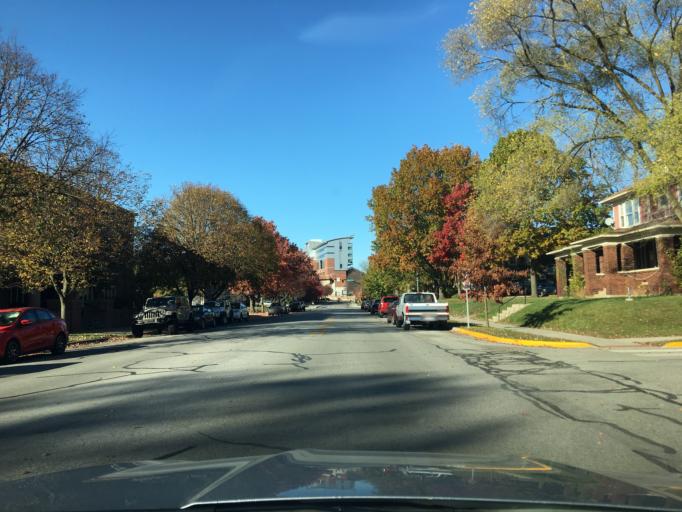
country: US
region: Indiana
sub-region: Tippecanoe County
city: West Lafayette
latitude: 40.4302
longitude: -86.9191
